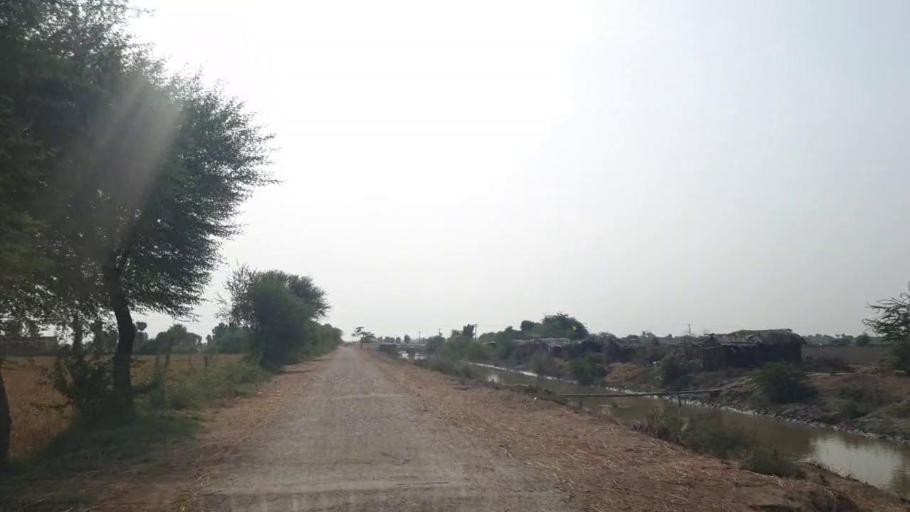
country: PK
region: Sindh
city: Badin
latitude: 24.7563
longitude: 68.7610
